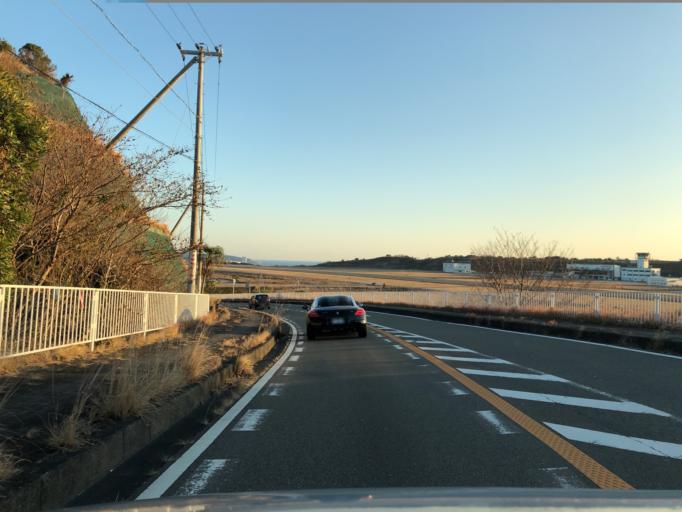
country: JP
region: Wakayama
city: Tanabe
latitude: 33.6683
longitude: 135.3624
